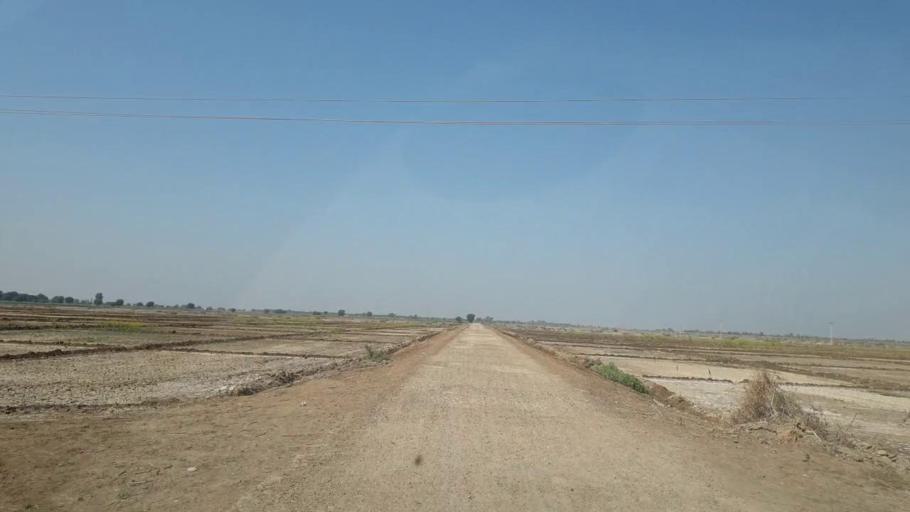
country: PK
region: Sindh
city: Mirpur Khas
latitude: 25.6910
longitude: 69.1157
